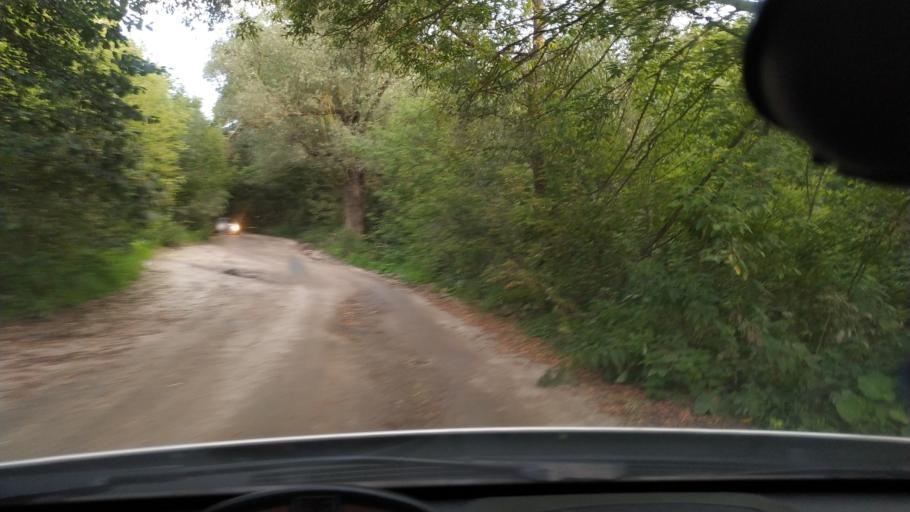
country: RU
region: Rjazan
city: Rybnoye
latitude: 54.8695
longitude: 39.6528
